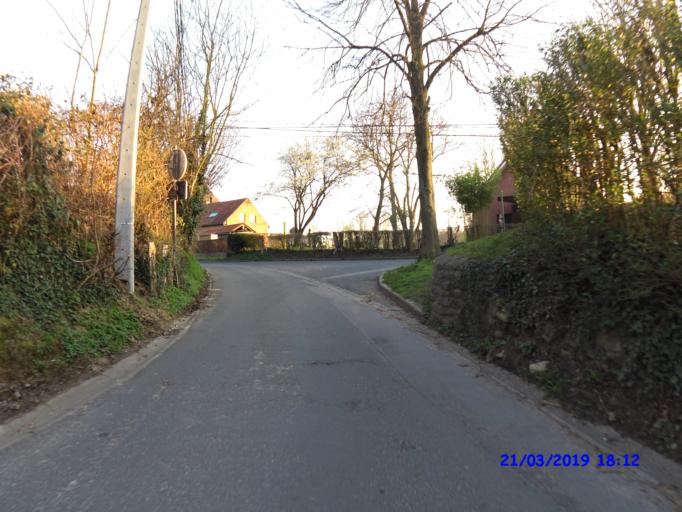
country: BE
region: Flanders
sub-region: Provincie Vlaams-Brabant
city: Linkebeek
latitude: 50.7707
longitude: 4.3444
